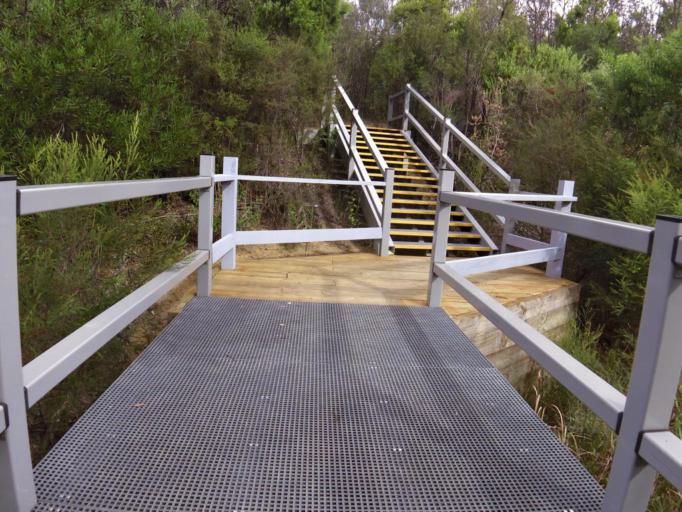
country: AU
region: Victoria
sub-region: Frankston
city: Frankston South
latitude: -38.1783
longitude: 145.1302
